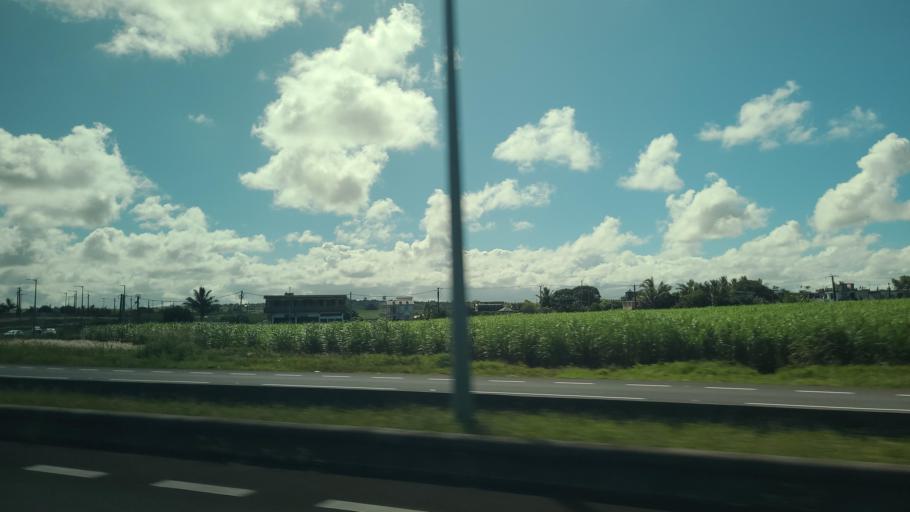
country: MU
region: Grand Port
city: Plaine Magnien
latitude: -20.4395
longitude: 57.6573
